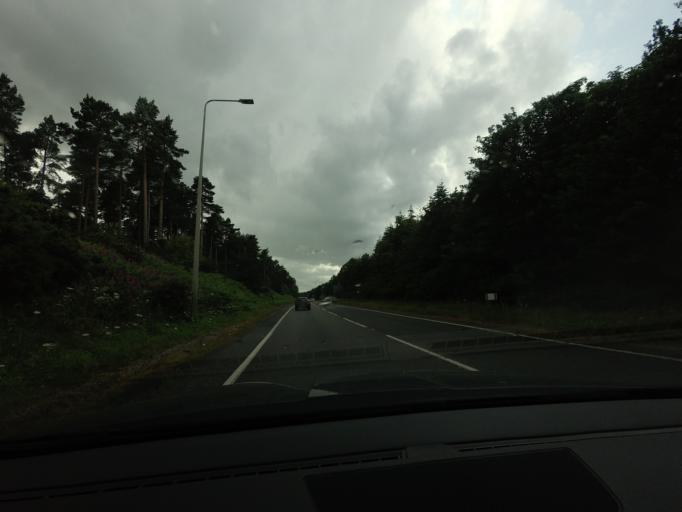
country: GB
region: Scotland
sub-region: Highland
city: Fortrose
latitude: 57.5301
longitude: -4.0493
